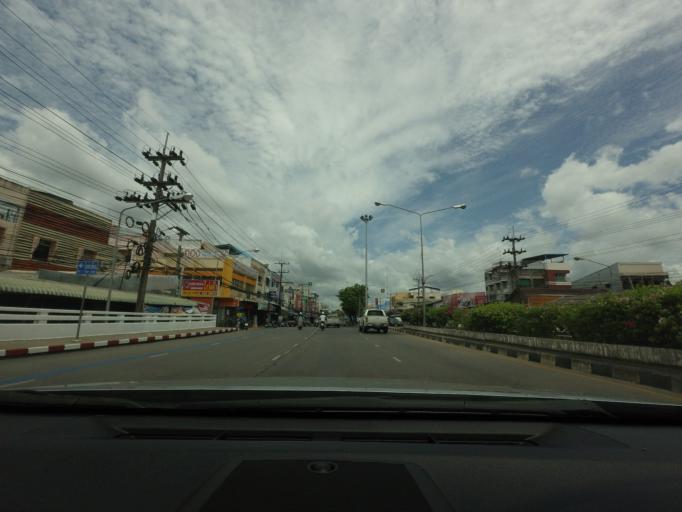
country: TH
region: Songkhla
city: Hat Yai
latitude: 7.0020
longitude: 100.4560
